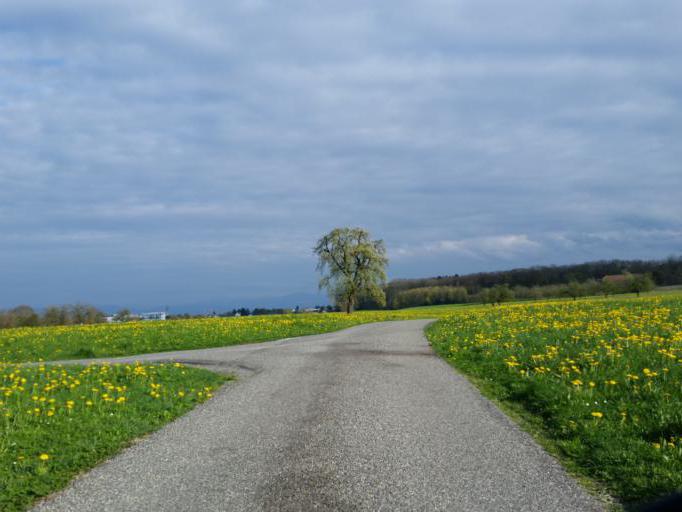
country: CH
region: Thurgau
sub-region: Arbon District
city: Uttwil
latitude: 47.5772
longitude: 9.3434
